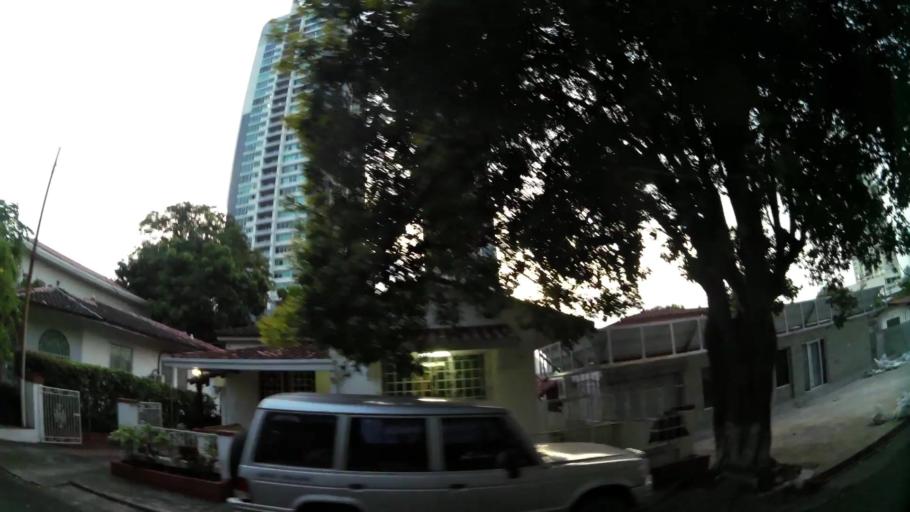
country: PA
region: Panama
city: Panama
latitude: 8.9893
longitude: -79.5100
